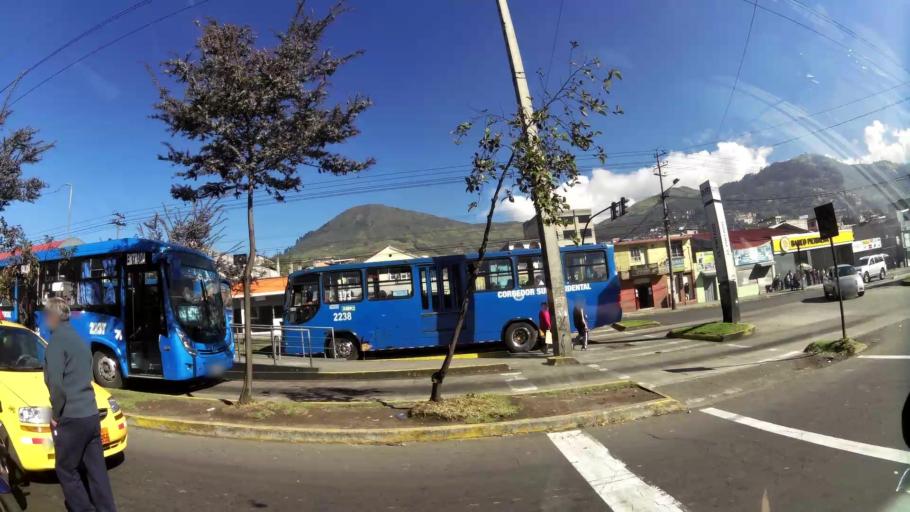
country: EC
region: Pichincha
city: Quito
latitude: -0.2455
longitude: -78.5339
